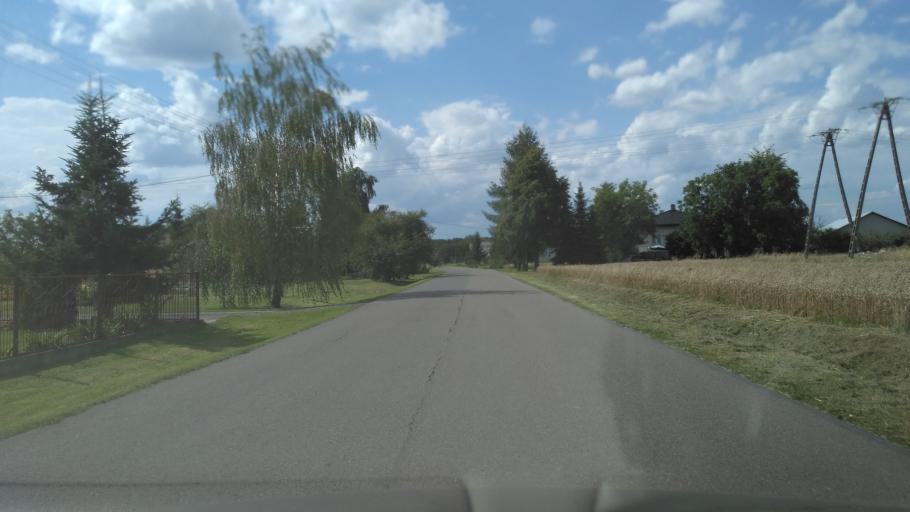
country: PL
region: Lublin Voivodeship
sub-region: Powiat leczynski
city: Milejow
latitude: 51.1865
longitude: 22.9473
